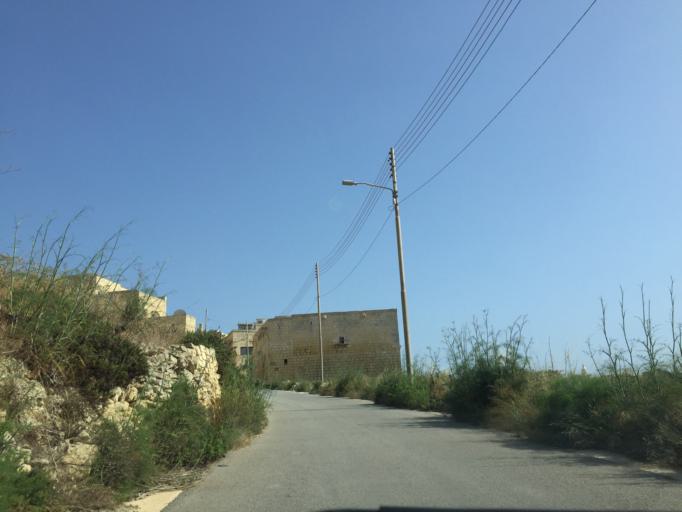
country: MT
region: L-Gharb
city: Gharb
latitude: 36.0653
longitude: 14.2062
